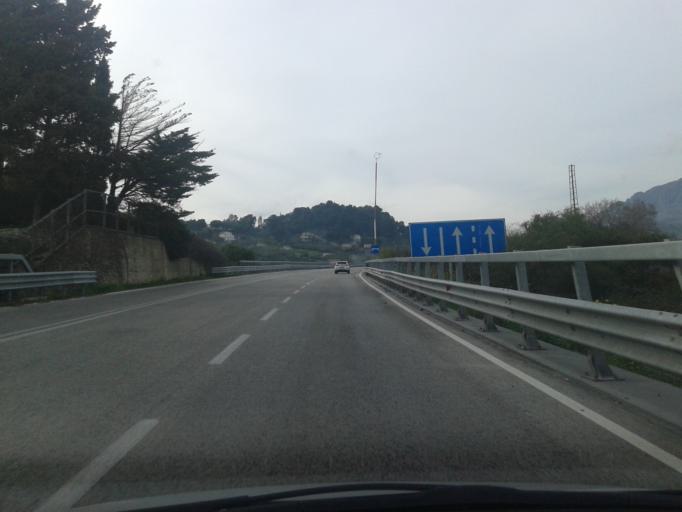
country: IT
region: Sicily
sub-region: Palermo
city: Giacalone
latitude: 38.0350
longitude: 13.2464
